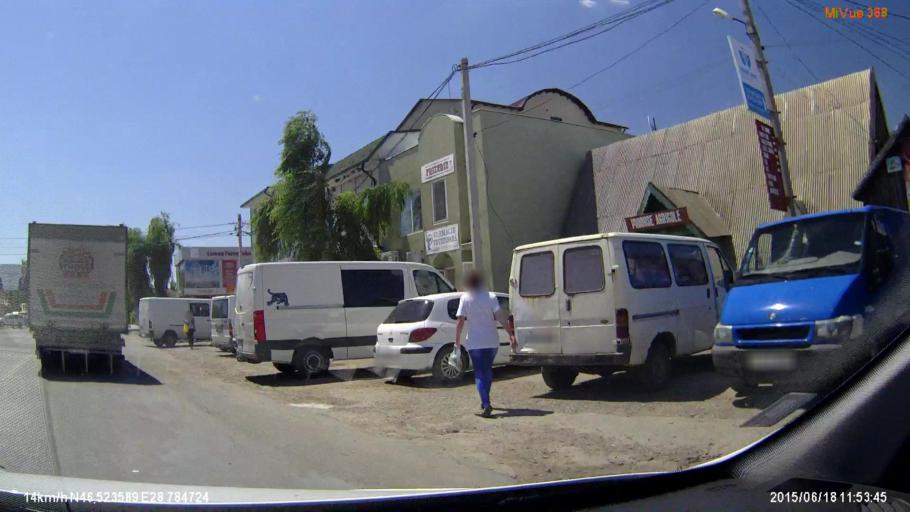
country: MD
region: Cimislia
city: Cimislia
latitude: 46.5237
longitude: 28.7847
